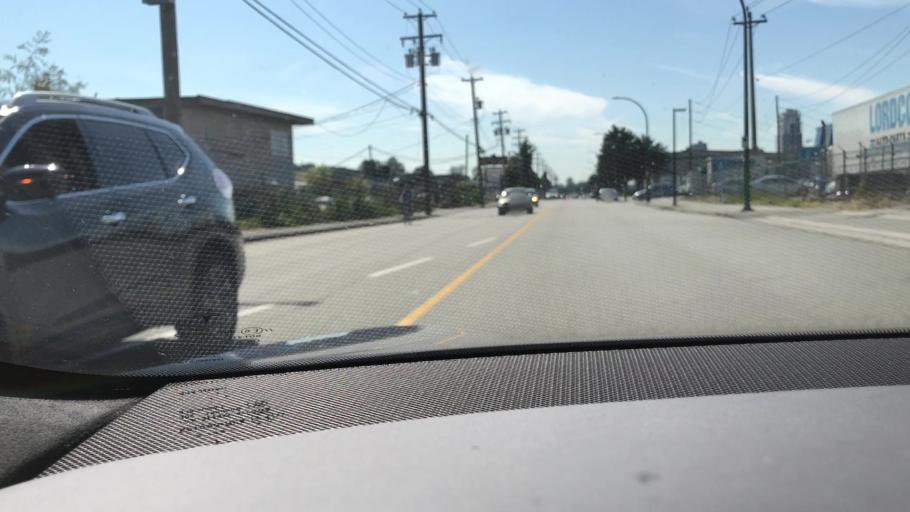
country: CA
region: British Columbia
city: Burnaby
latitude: 49.2608
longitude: -122.9857
